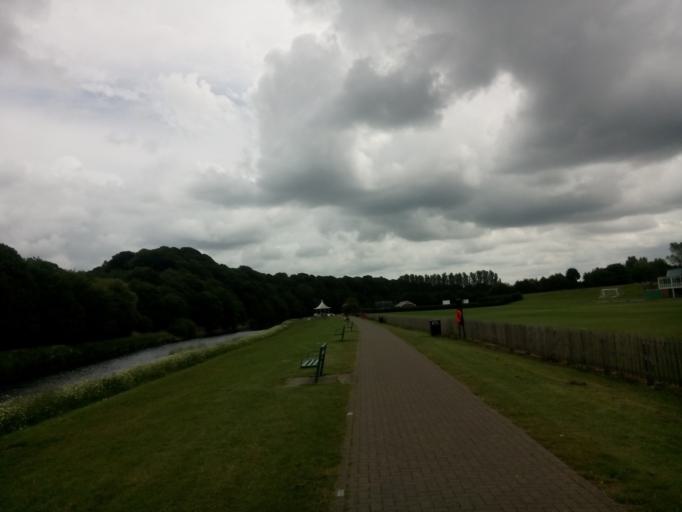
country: GB
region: England
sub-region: County Durham
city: Durham
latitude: 54.7758
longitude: -1.5660
